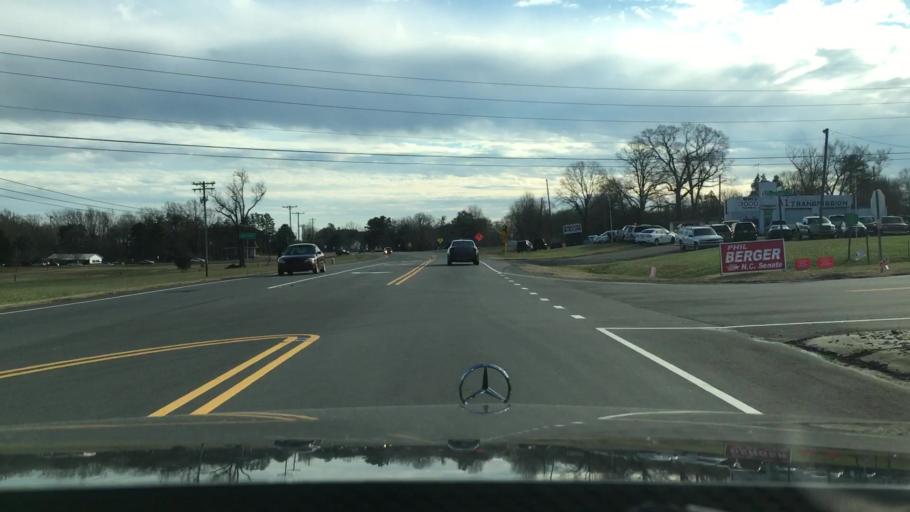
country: US
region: Virginia
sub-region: City of Danville
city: Danville
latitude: 36.5342
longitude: -79.3999
